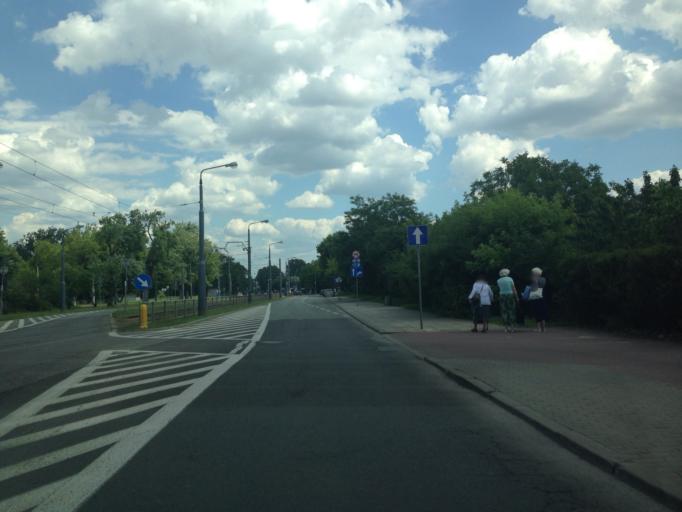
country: PL
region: Masovian Voivodeship
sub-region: Warszawa
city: Bemowo
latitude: 52.2468
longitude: 20.9355
